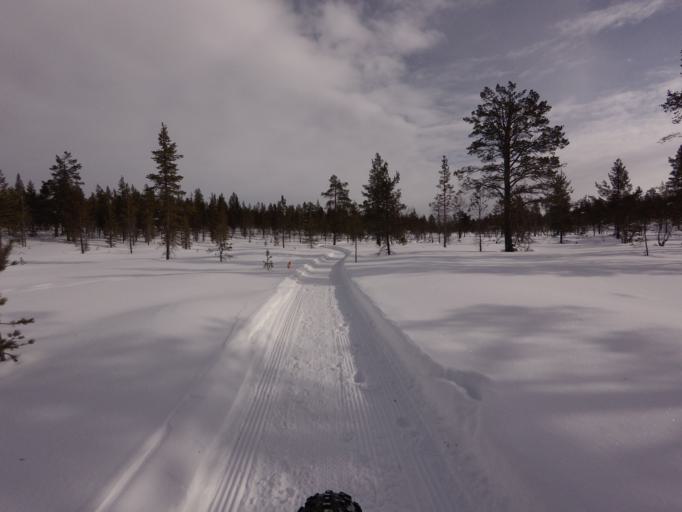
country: FI
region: Lapland
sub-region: Pohjois-Lappi
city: Ivalo
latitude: 68.3444
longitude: 27.4409
